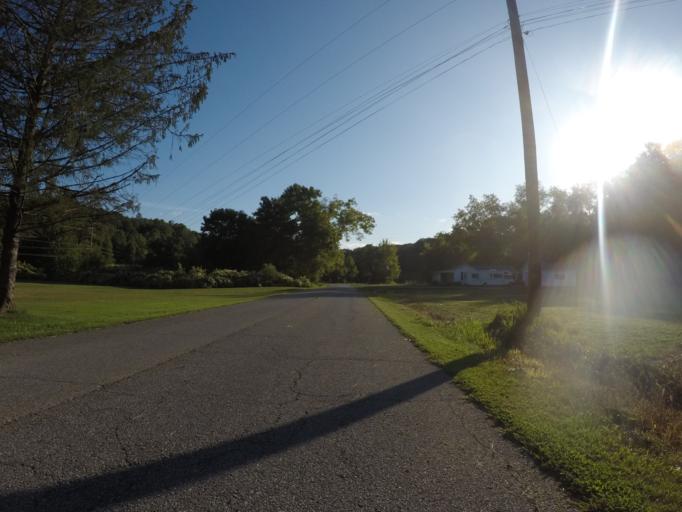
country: US
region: Ohio
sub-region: Lawrence County
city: Coal Grove
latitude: 38.5360
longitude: -82.5425
